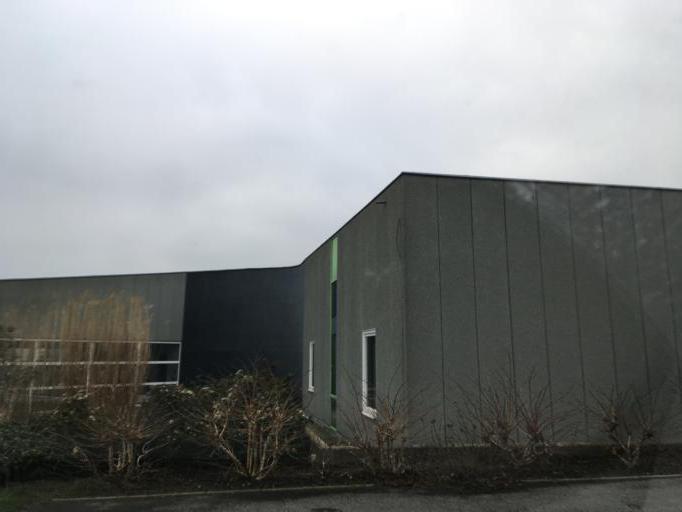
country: BE
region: Flanders
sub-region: Provincie West-Vlaanderen
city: Hooglede
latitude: 50.9953
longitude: 3.1208
